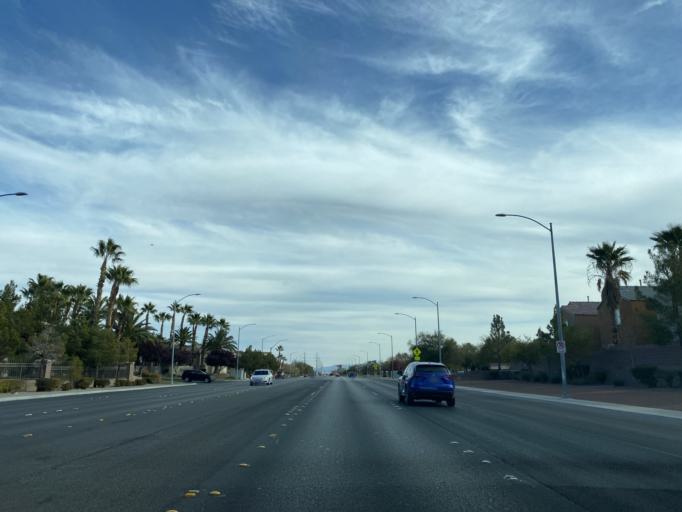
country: US
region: Nevada
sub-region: Clark County
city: Enterprise
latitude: 36.0554
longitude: -115.2902
